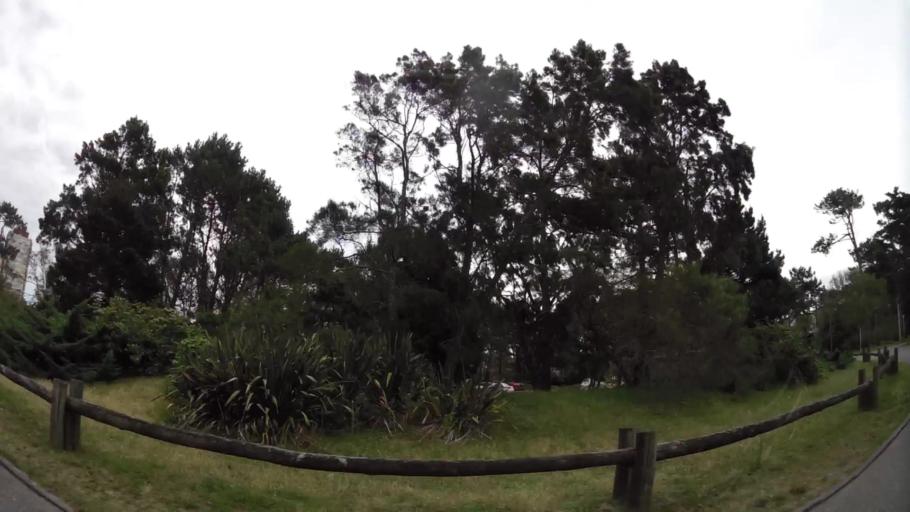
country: UY
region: Maldonado
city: Punta del Este
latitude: -34.9446
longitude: -54.9385
